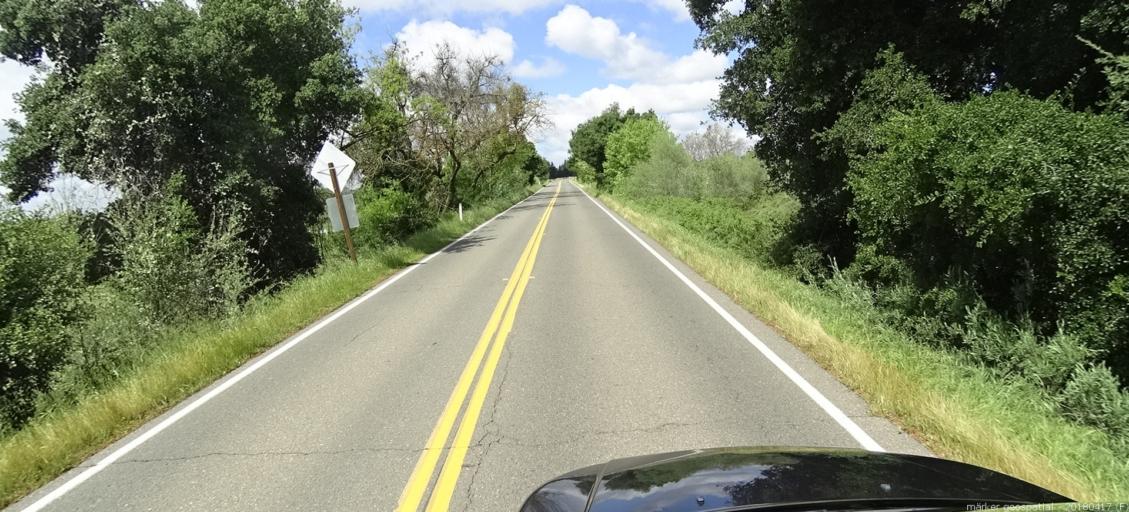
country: US
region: California
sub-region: Sacramento County
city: Walnut Grove
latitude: 38.2376
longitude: -121.5319
